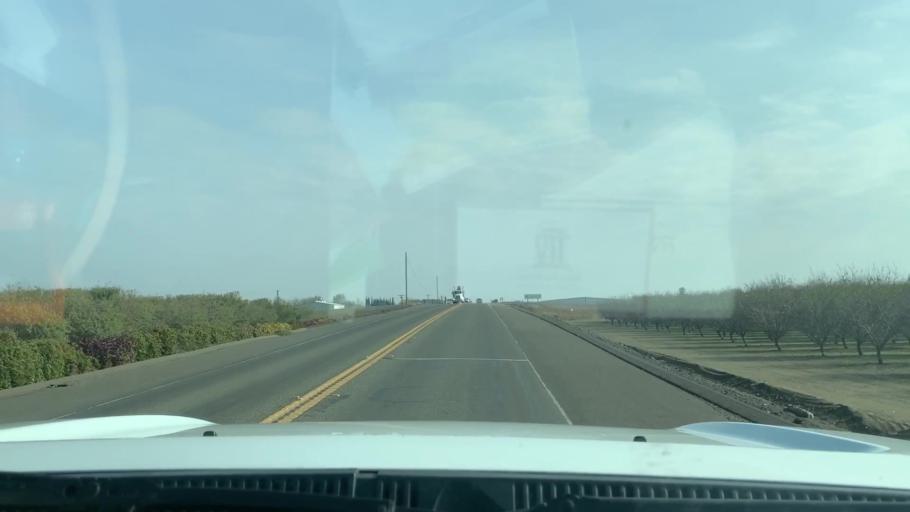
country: US
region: California
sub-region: Fresno County
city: Huron
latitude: 36.2553
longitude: -120.0927
